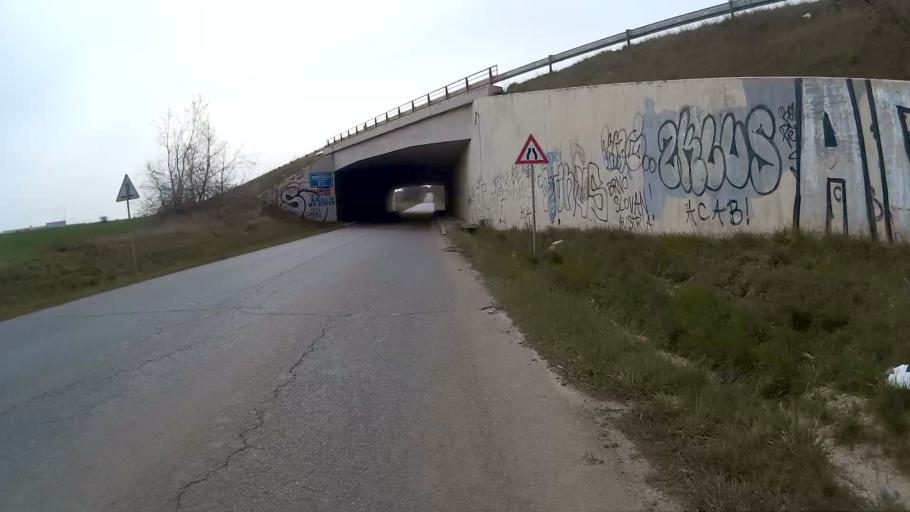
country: CZ
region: South Moravian
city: Rajhrad
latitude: 49.0816
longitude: 16.5694
